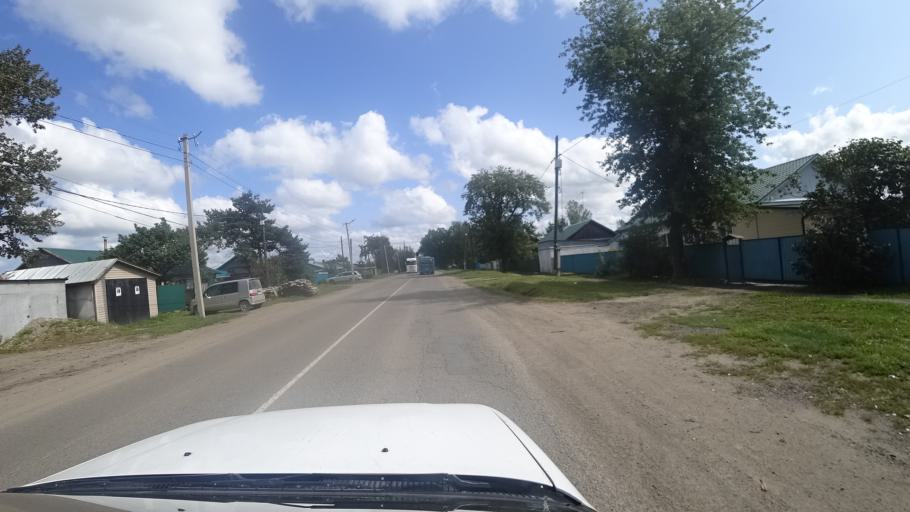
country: RU
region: Primorskiy
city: Dal'nerechensk
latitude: 45.9286
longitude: 133.7644
